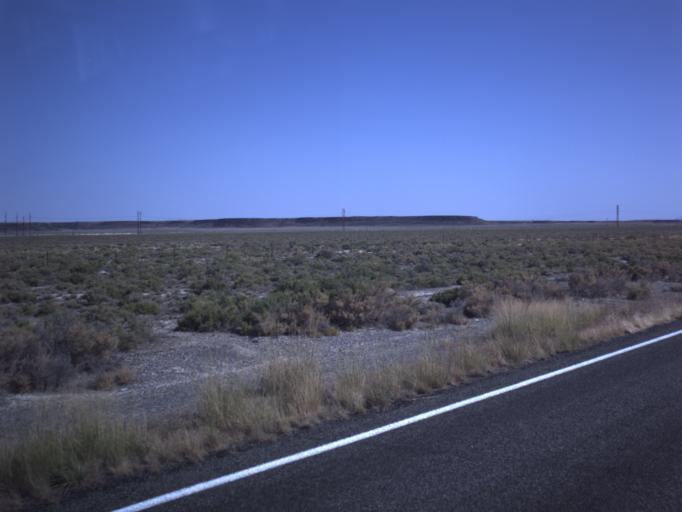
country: US
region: Utah
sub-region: Millard County
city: Delta
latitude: 39.1433
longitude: -112.7234
